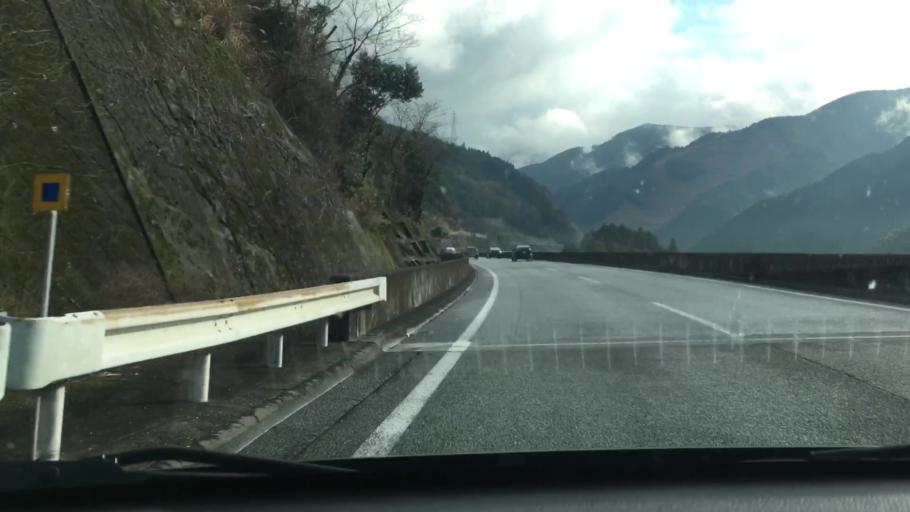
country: JP
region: Kumamoto
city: Yatsushiro
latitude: 32.4114
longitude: 130.6957
